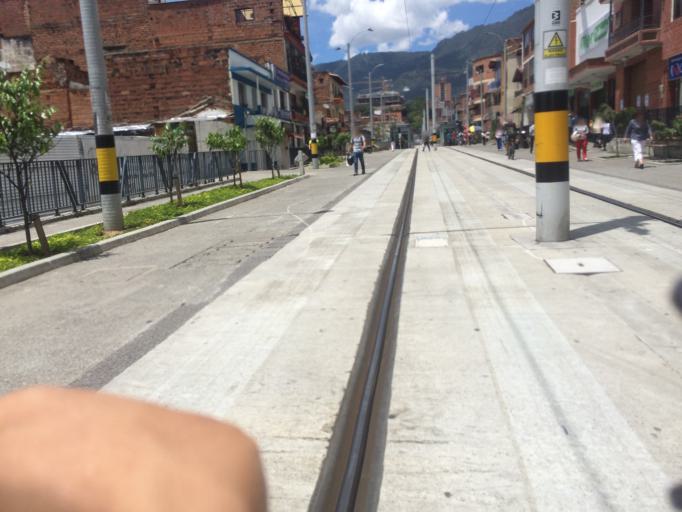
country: CO
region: Antioquia
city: Medellin
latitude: 6.2420
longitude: -75.5551
